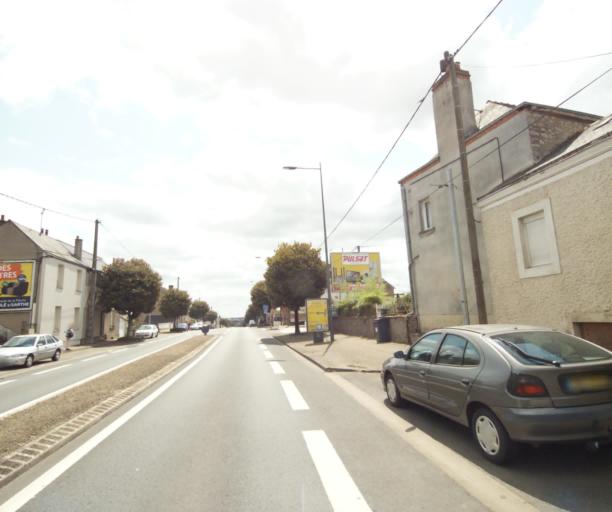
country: FR
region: Pays de la Loire
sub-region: Departement de la Sarthe
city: Sable-sur-Sarthe
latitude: 47.8469
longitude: -0.3465
